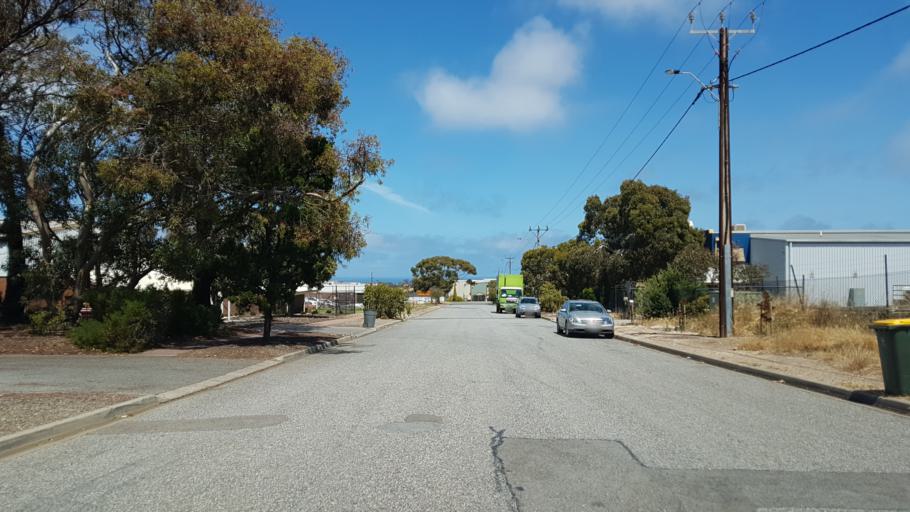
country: AU
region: South Australia
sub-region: Onkaparinga
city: Morphett Vale
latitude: -35.1149
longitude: 138.5031
